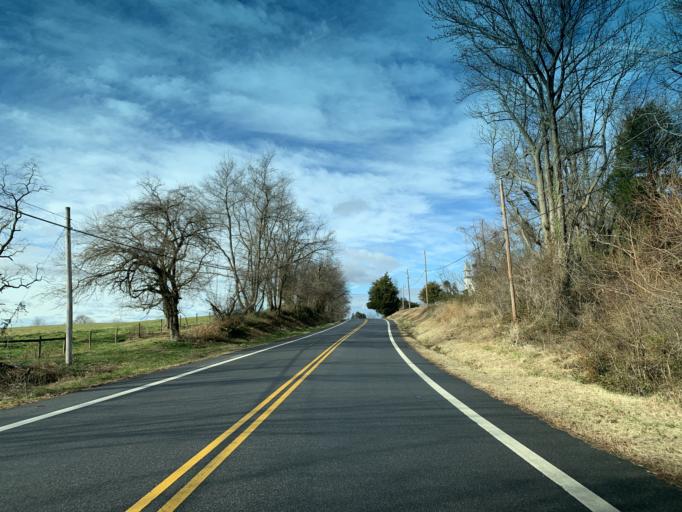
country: US
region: Maryland
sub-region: Kent County
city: Chestertown
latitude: 39.3288
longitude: -76.0547
